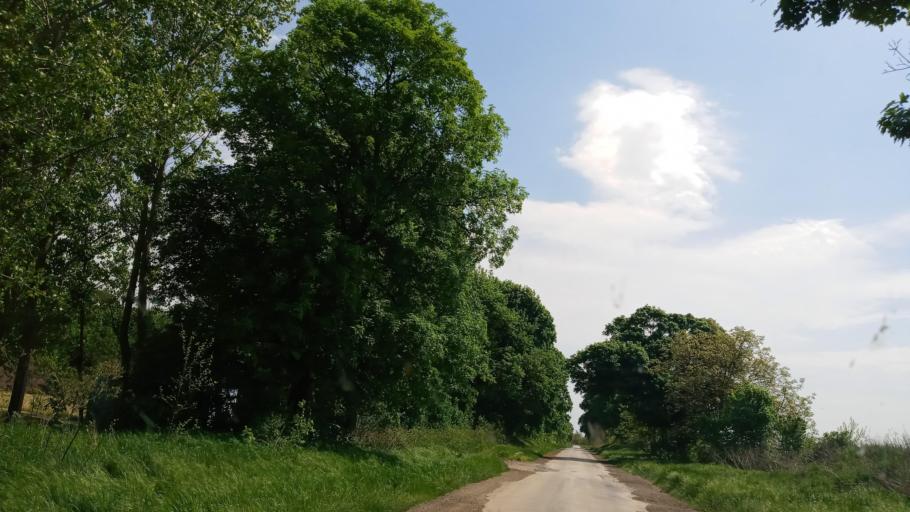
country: HU
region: Baranya
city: Villany
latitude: 45.8273
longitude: 18.5027
